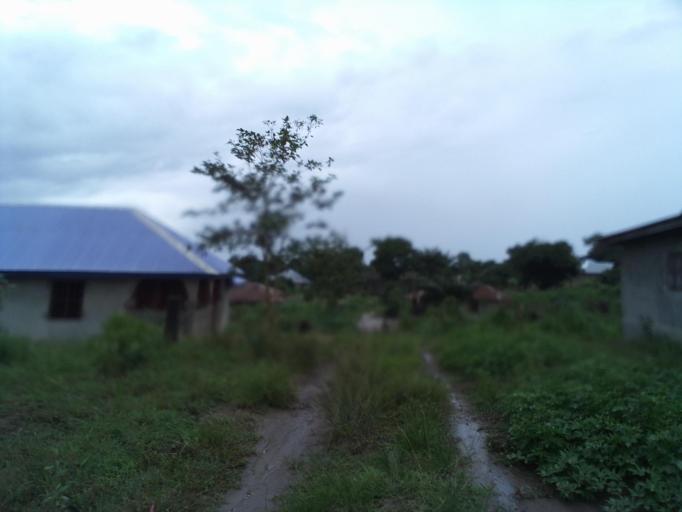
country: SL
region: Eastern Province
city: Kenema
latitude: 7.8779
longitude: -11.1561
